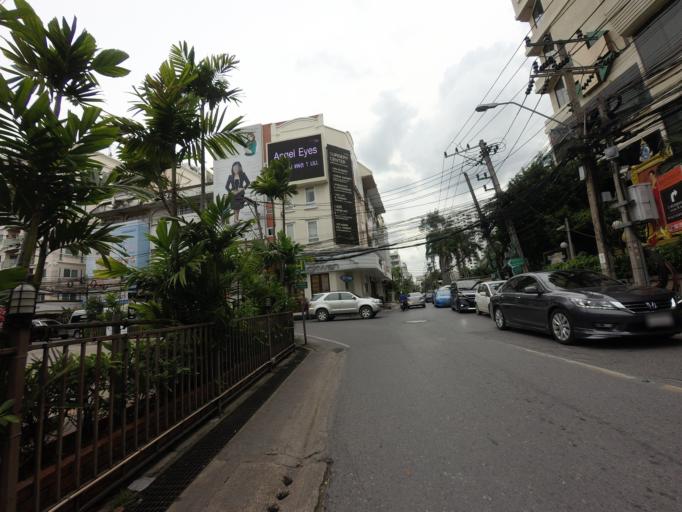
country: TH
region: Bangkok
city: Watthana
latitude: 13.7348
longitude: 100.5772
